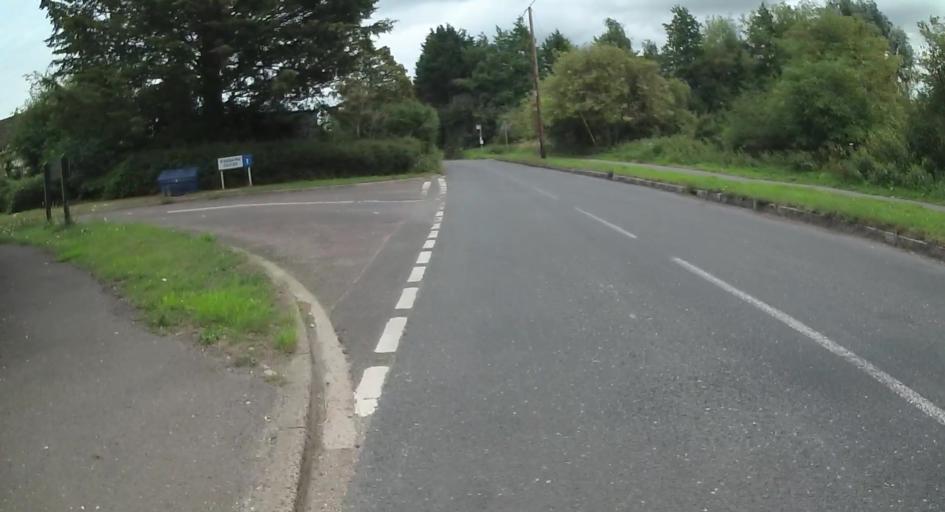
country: GB
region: England
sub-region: Hampshire
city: Swanmore
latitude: 51.0500
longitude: -1.1643
